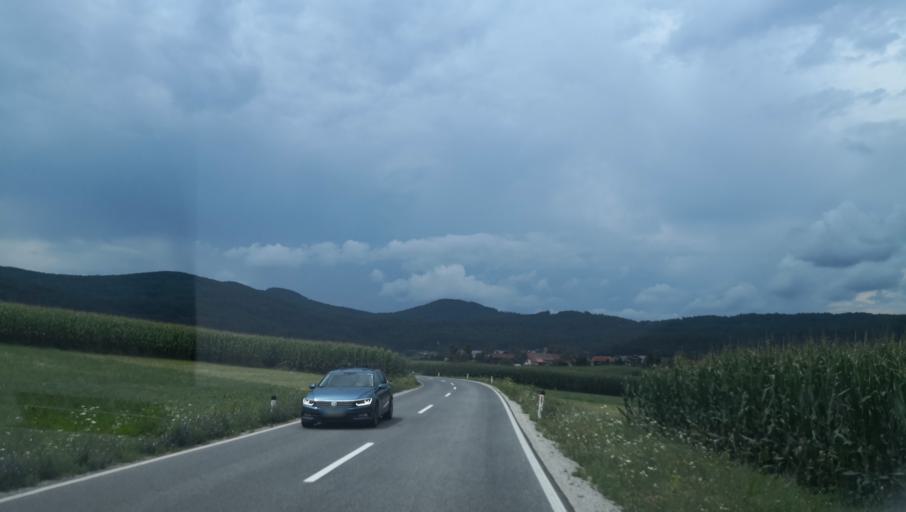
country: SI
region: Ivancna Gorica
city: Ivancna Gorica
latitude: 45.8876
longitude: 14.7940
